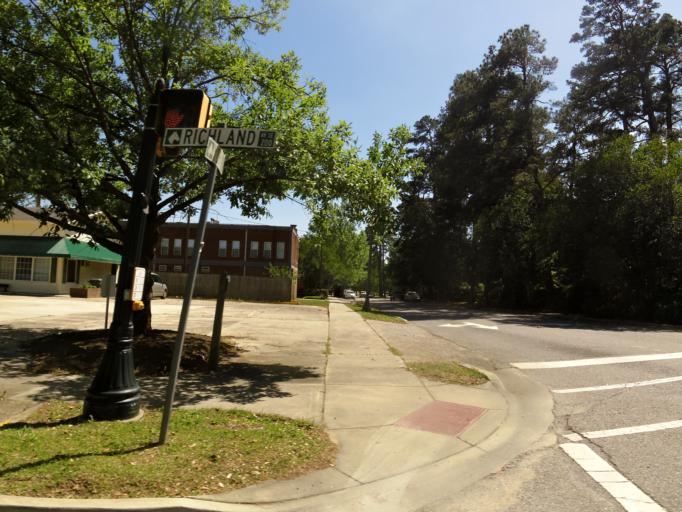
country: US
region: South Carolina
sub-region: Aiken County
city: Aiken
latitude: 33.5600
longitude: -81.7178
